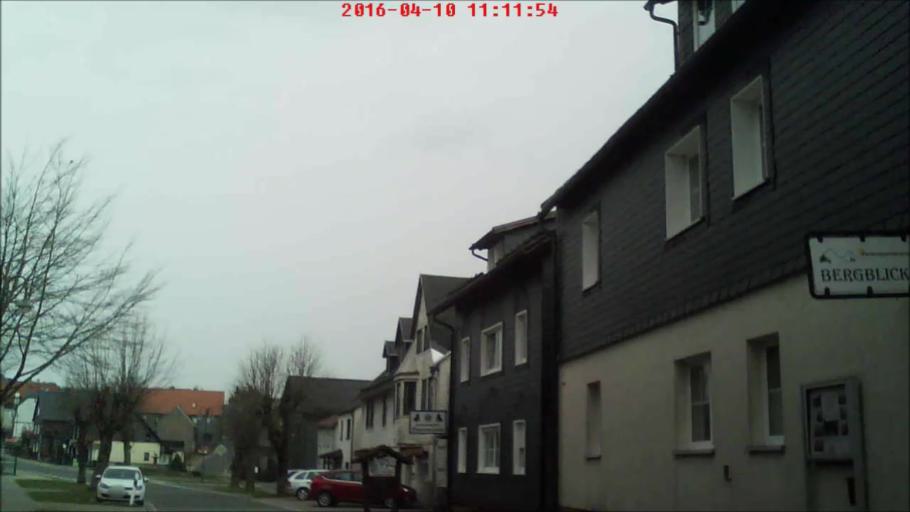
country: DE
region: Thuringia
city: Frauenwald
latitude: 50.5811
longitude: 10.8598
